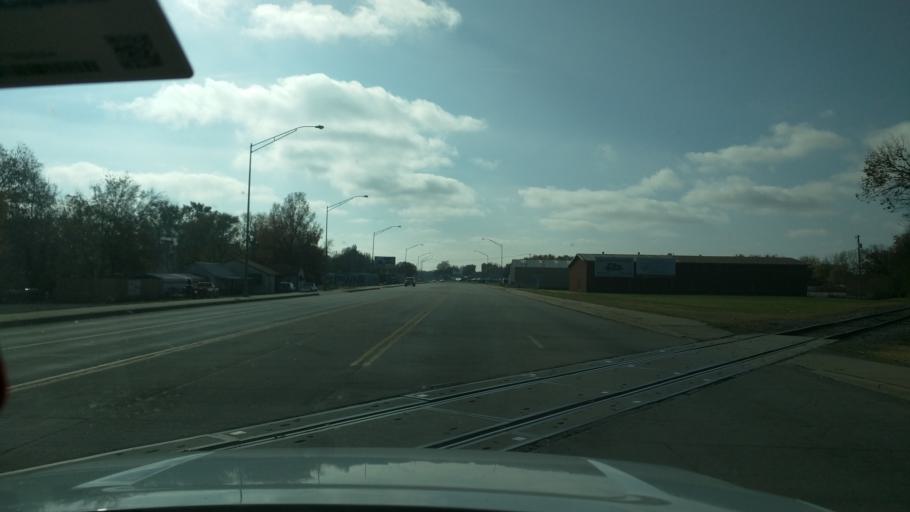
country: US
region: Oklahoma
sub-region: Washington County
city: Dewey
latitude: 36.7962
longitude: -95.9357
